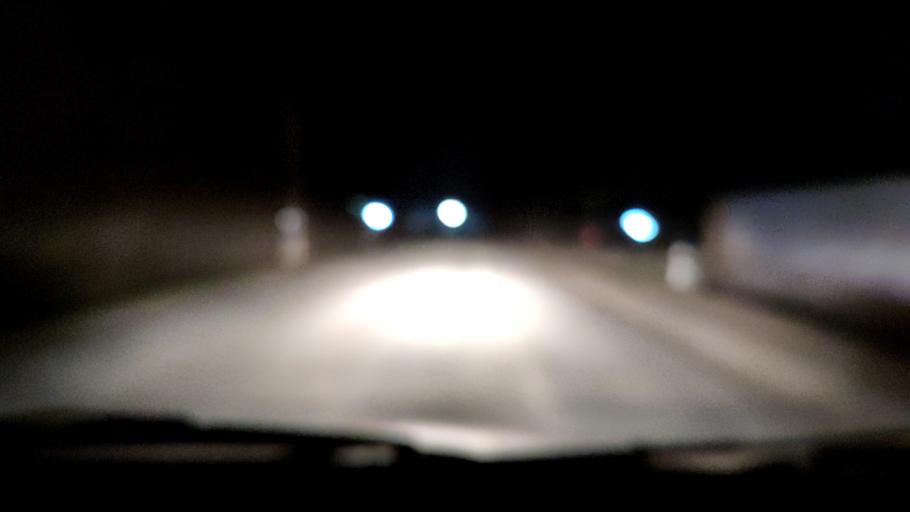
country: RU
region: Voronezj
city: Podkletnoye
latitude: 51.6412
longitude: 39.4930
